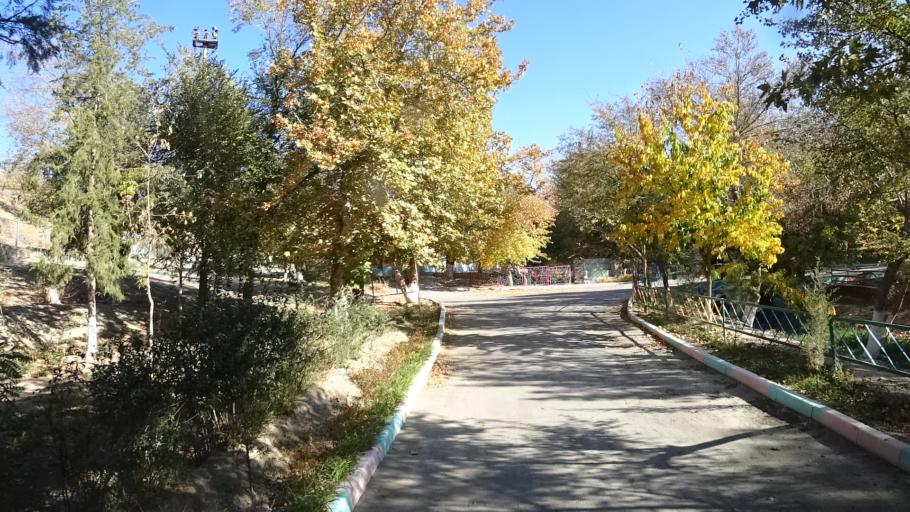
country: UZ
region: Navoiy
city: Karmana Shahri
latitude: 40.2913
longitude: 65.6009
